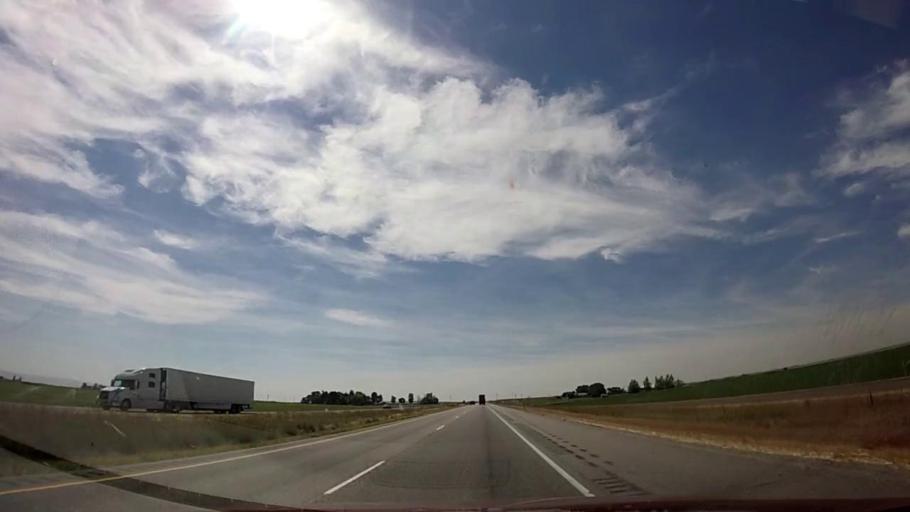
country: US
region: Idaho
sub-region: Cassia County
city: Burley
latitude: 42.5764
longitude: -113.9851
